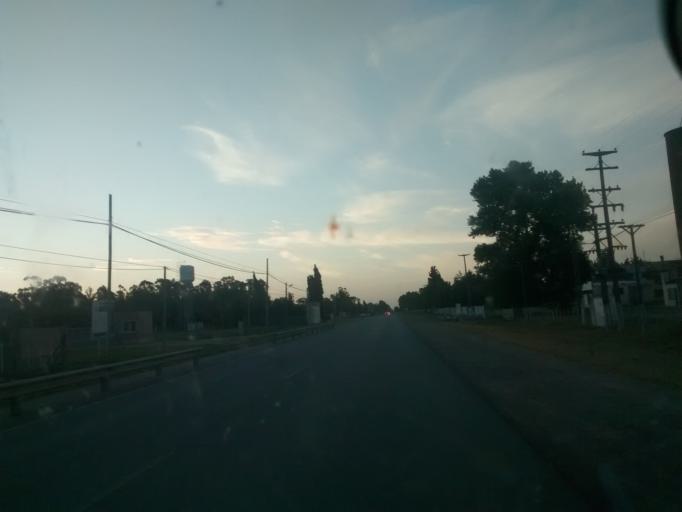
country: AR
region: Buenos Aires
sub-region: Partido de Loberia
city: Loberia
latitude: -38.1894
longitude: -58.7490
